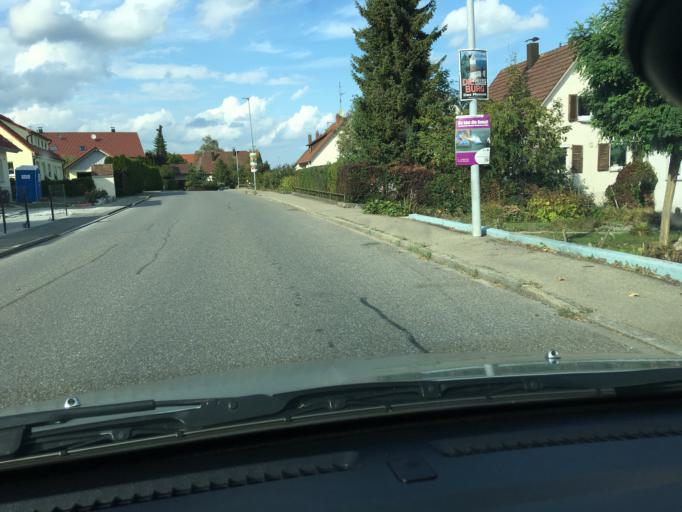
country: DE
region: Baden-Wuerttemberg
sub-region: Tuebingen Region
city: Aulendorf
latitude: 47.9739
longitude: 9.6431
